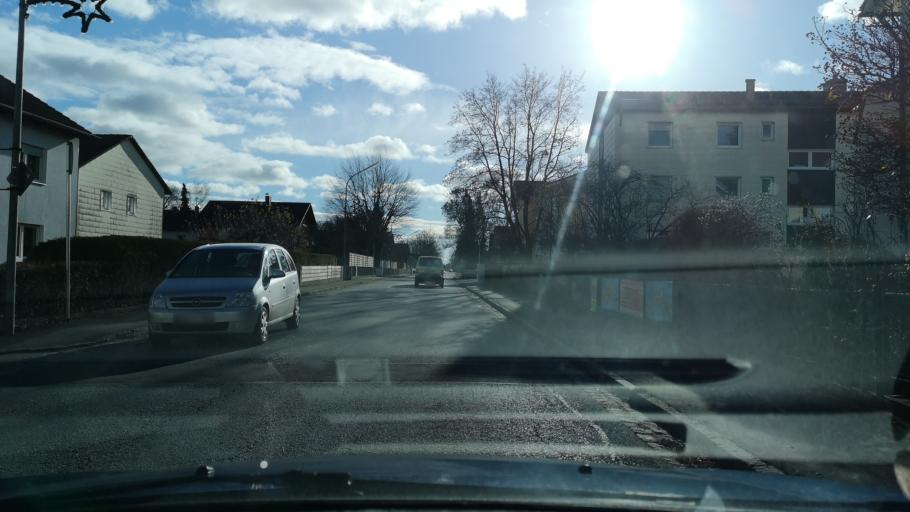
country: DE
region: Bavaria
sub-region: Upper Bavaria
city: Poing
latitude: 48.1686
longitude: 11.8121
